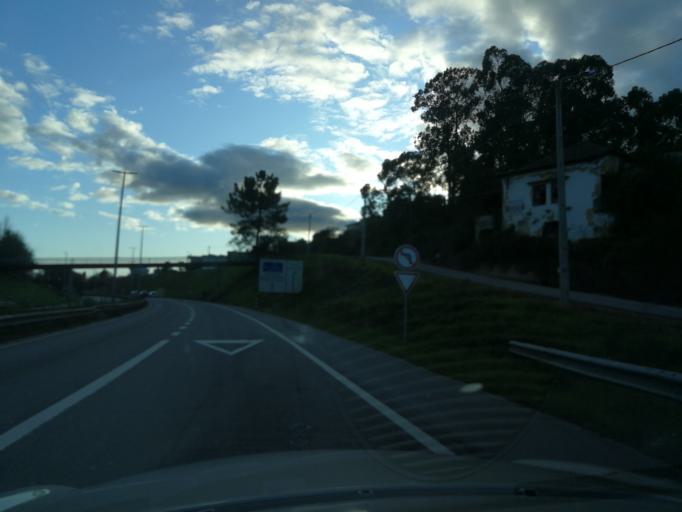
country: PT
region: Braga
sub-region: Barcelos
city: Vila Frescainha
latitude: 41.5342
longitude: -8.6390
